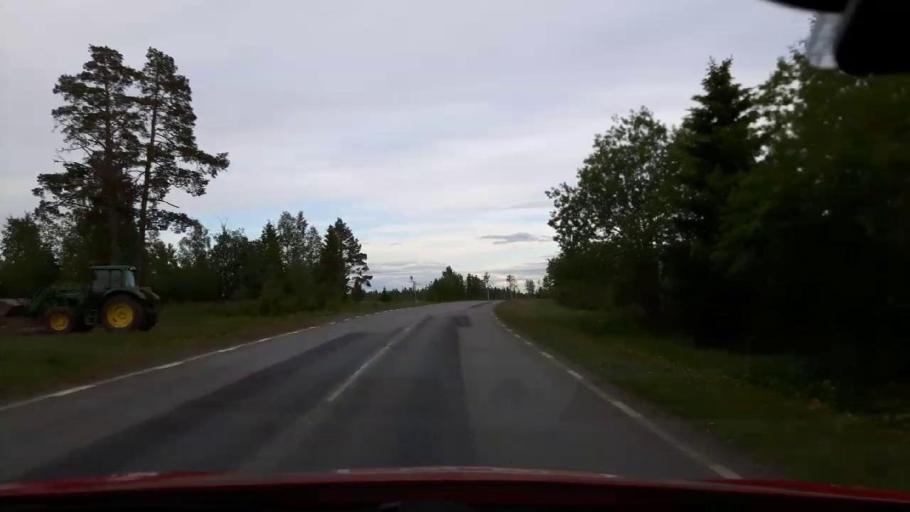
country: SE
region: Jaemtland
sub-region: OEstersunds Kommun
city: Ostersund
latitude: 63.0804
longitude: 14.4432
